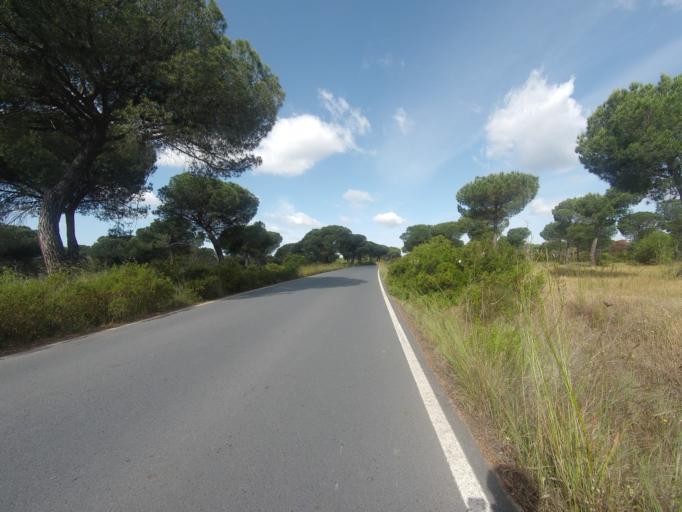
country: ES
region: Andalusia
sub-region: Provincia de Huelva
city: Aljaraque
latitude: 37.2472
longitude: -7.0230
